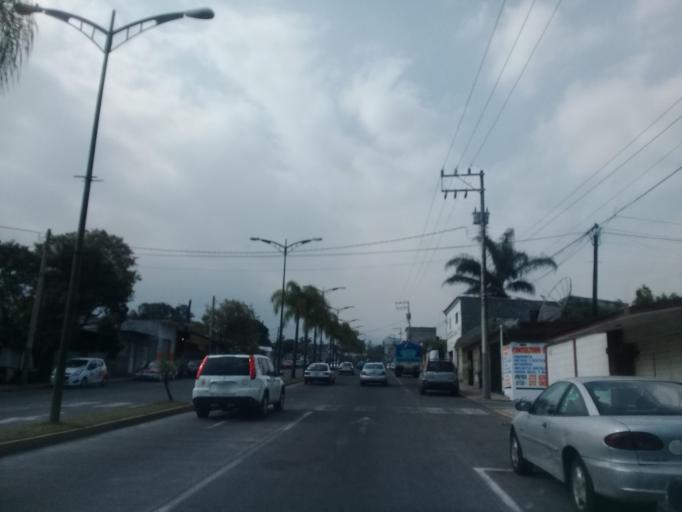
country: MX
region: Veracruz
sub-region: Ixhuatlancillo
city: Union y Progreso
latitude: 18.8670
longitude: -97.1124
